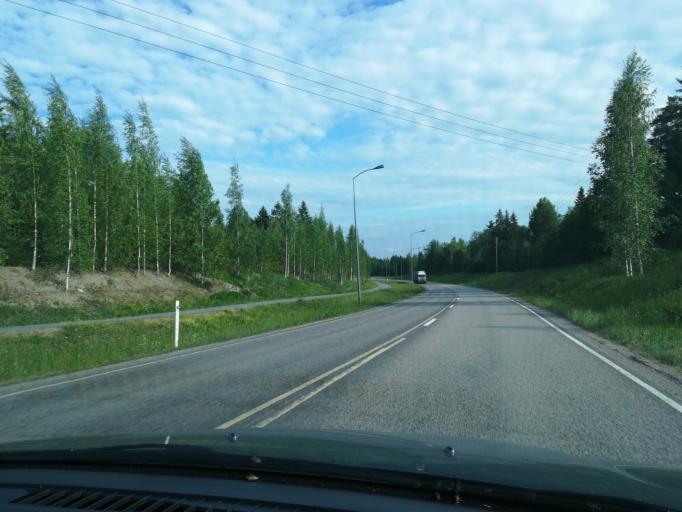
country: FI
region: South Karelia
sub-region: Imatra
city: Imatra
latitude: 61.1607
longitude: 28.7901
